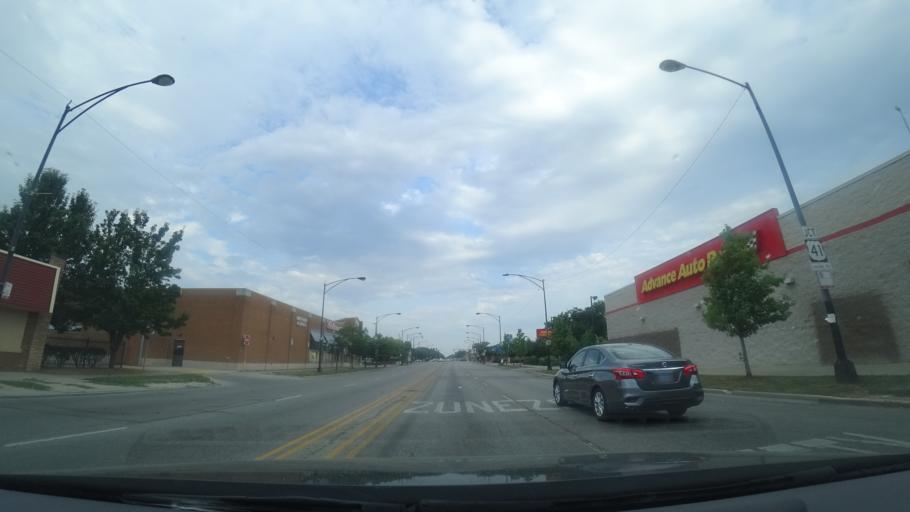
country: US
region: Illinois
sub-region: Cook County
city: Lincolnwood
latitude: 41.9904
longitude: -87.7043
